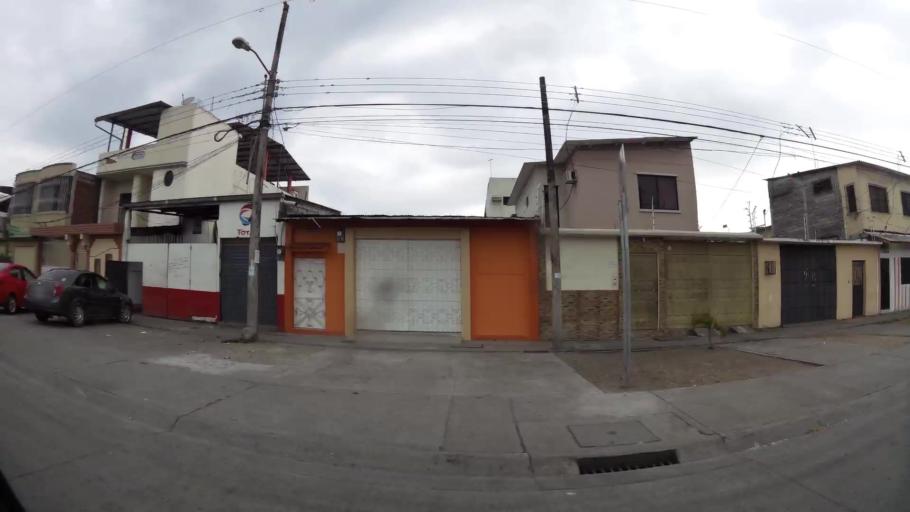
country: EC
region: Guayas
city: Eloy Alfaro
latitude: -2.1215
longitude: -79.8830
